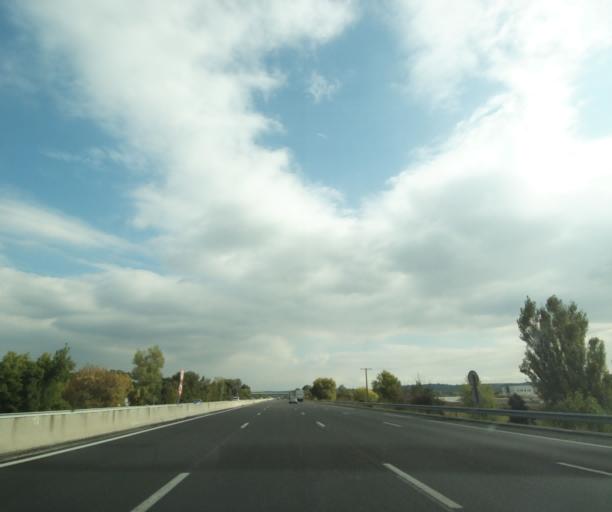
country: FR
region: Provence-Alpes-Cote d'Azur
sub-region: Departement des Bouches-du-Rhone
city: Pelissanne
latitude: 43.6192
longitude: 5.1356
